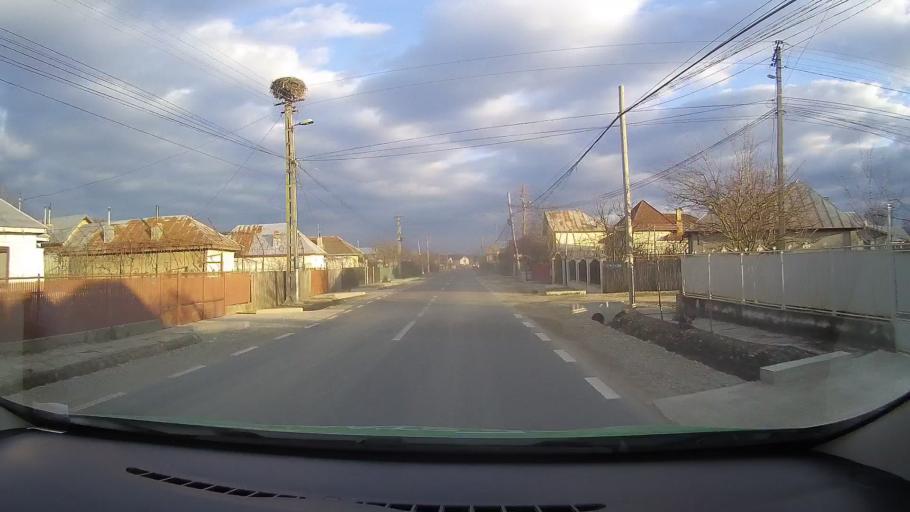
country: RO
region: Dambovita
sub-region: Comuna I. L. Caragiale
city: Ghirdoveni
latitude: 44.9417
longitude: 25.6695
